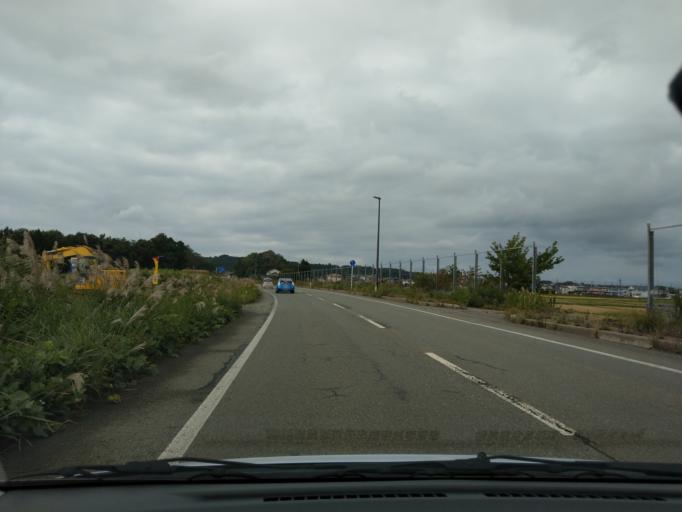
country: JP
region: Akita
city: Akita Shi
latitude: 39.6697
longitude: 140.1015
